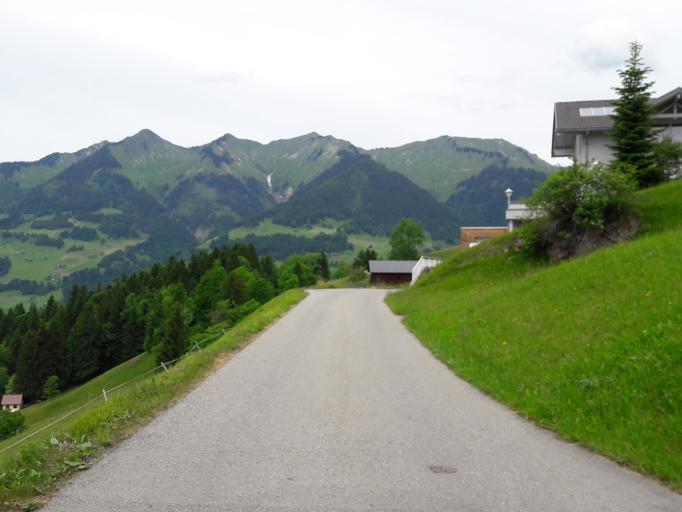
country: AT
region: Vorarlberg
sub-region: Politischer Bezirk Bludenz
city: Ludesch
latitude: 47.1984
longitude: 9.8072
